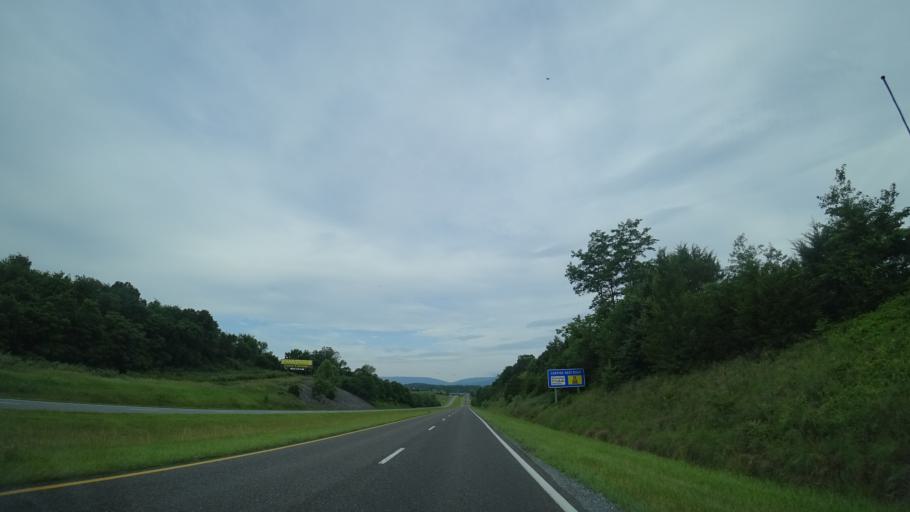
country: US
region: Virginia
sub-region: Page County
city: Luray
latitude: 38.6758
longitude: -78.4391
